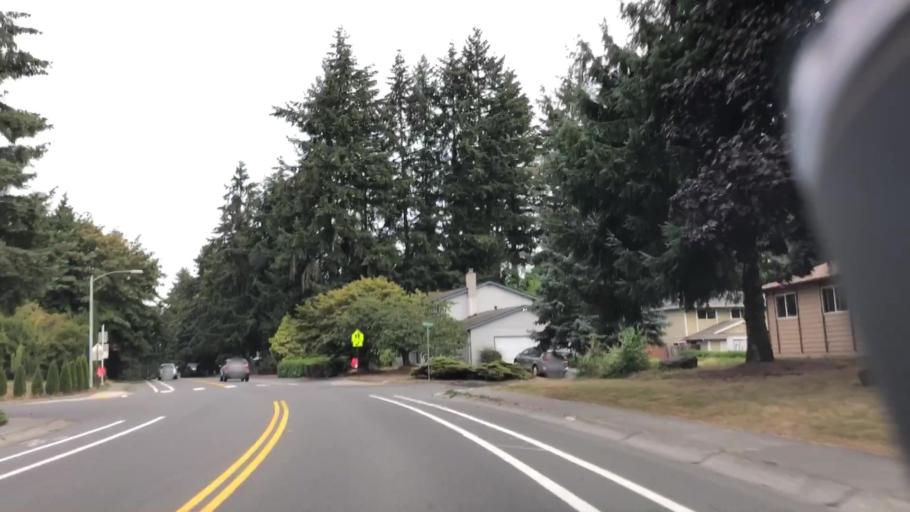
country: US
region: Washington
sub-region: King County
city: Kingsgate
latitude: 47.7304
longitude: -122.1680
